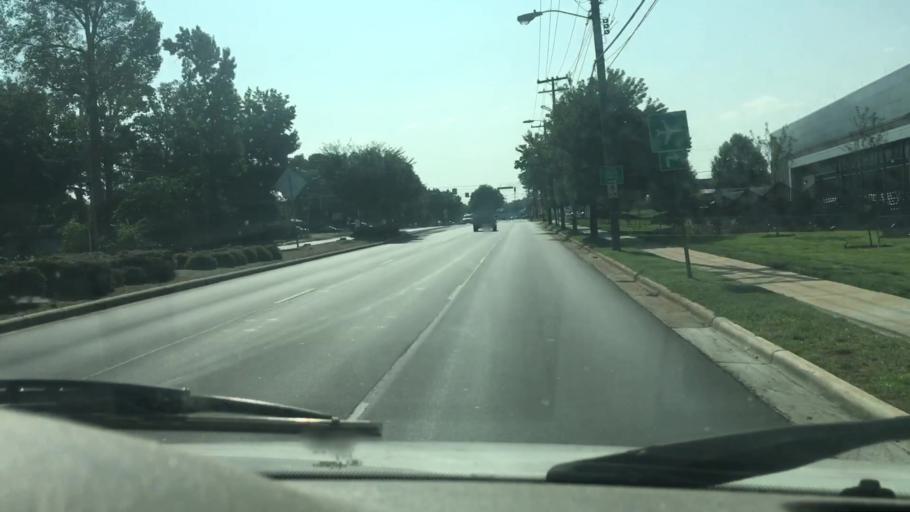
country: US
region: North Carolina
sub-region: Mecklenburg County
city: Charlotte
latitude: 35.2269
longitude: -80.9117
